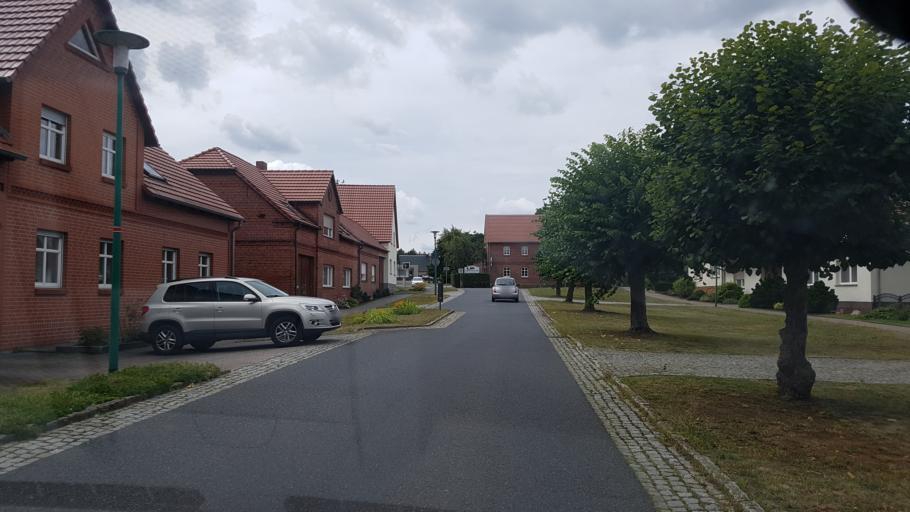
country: DE
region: Brandenburg
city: Spremberg
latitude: 51.5086
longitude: 14.4008
